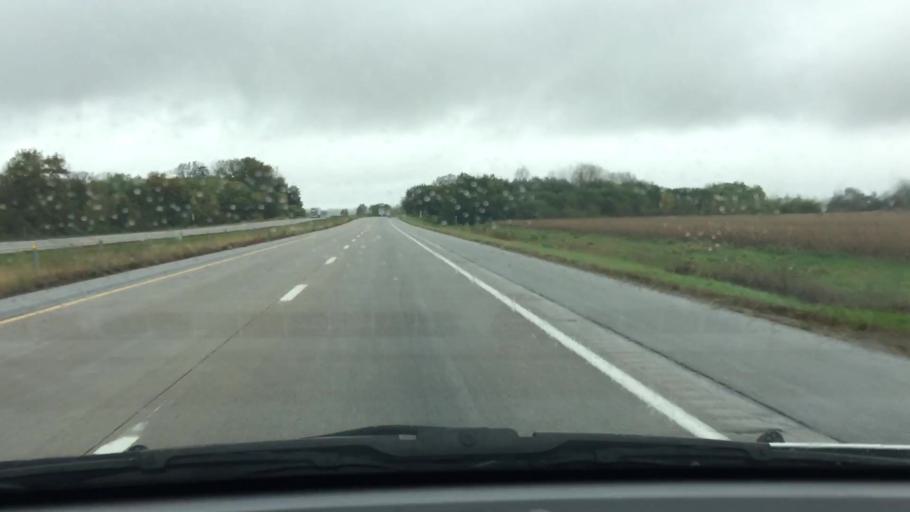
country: US
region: Iowa
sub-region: Jasper County
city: Colfax
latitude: 41.6962
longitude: -93.1936
